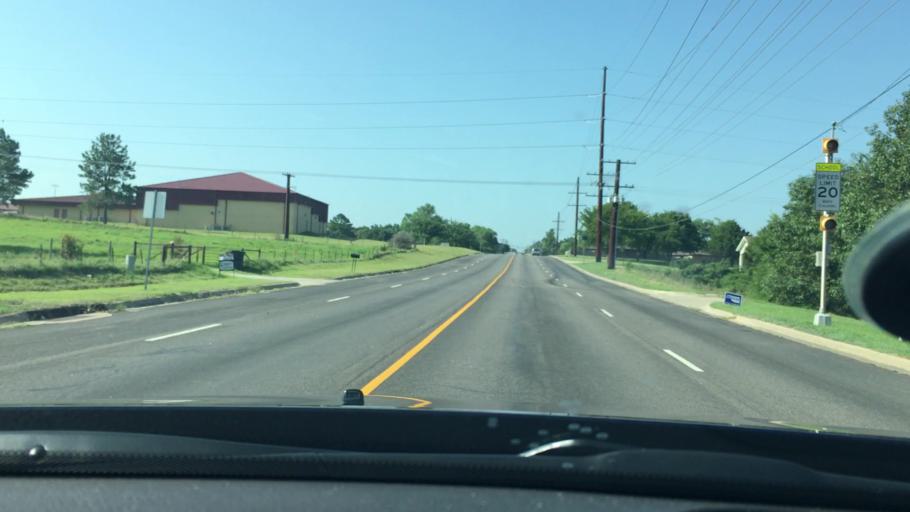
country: US
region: Oklahoma
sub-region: Pontotoc County
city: Ada
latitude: 34.7898
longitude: -96.6348
